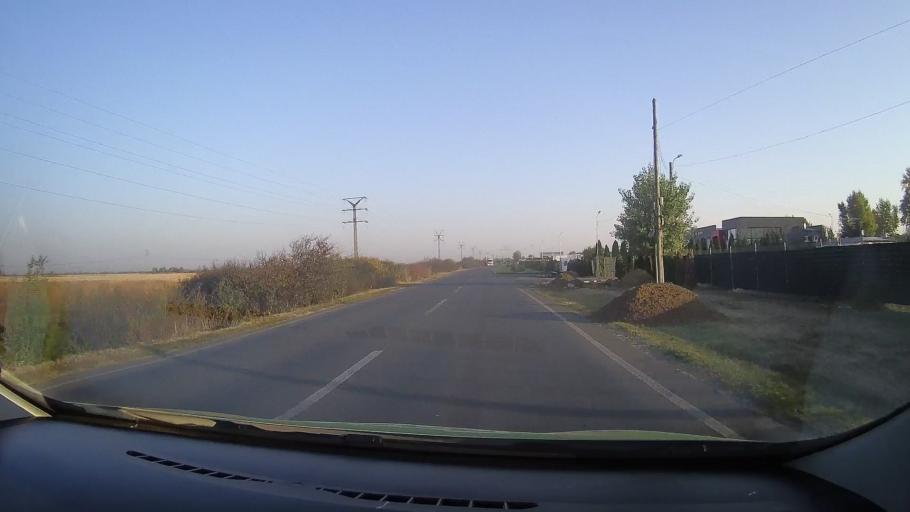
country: RO
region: Arad
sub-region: Comuna Sofronea
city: Sofronea
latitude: 46.2287
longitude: 21.3204
